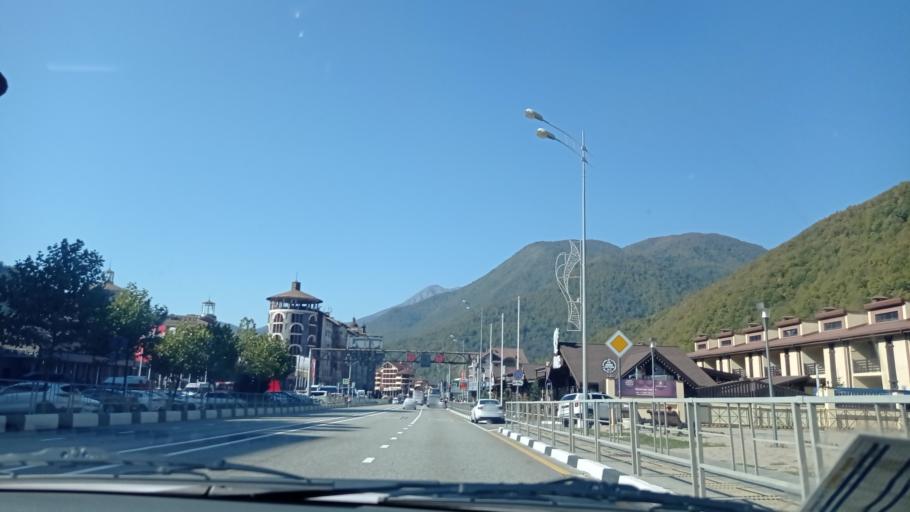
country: RU
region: Krasnodarskiy
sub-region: Sochi City
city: Krasnaya Polyana
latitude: 43.6833
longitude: 40.2691
